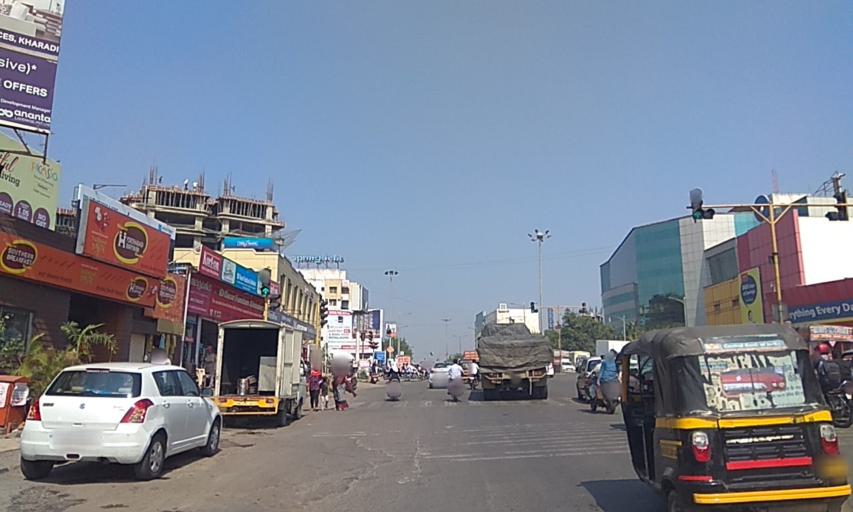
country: IN
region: Maharashtra
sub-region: Pune Division
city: Lohogaon
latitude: 18.5504
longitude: 73.9369
